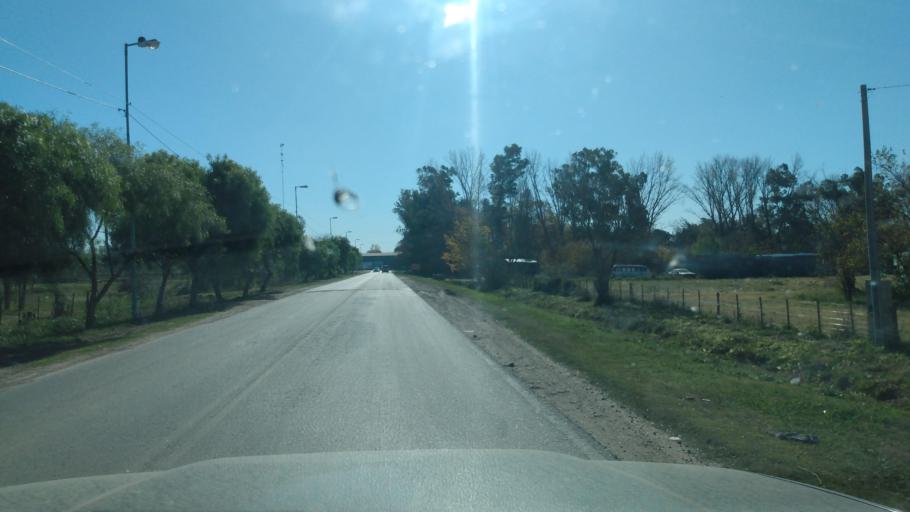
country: AR
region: Buenos Aires
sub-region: Partido de Lujan
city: Lujan
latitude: -34.4862
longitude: -59.2144
